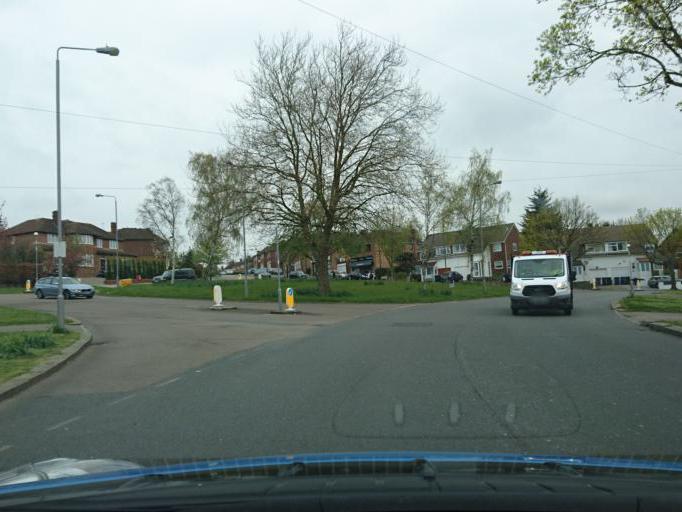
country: GB
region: England
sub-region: Greater London
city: Barnet
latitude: 51.6214
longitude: -0.1906
